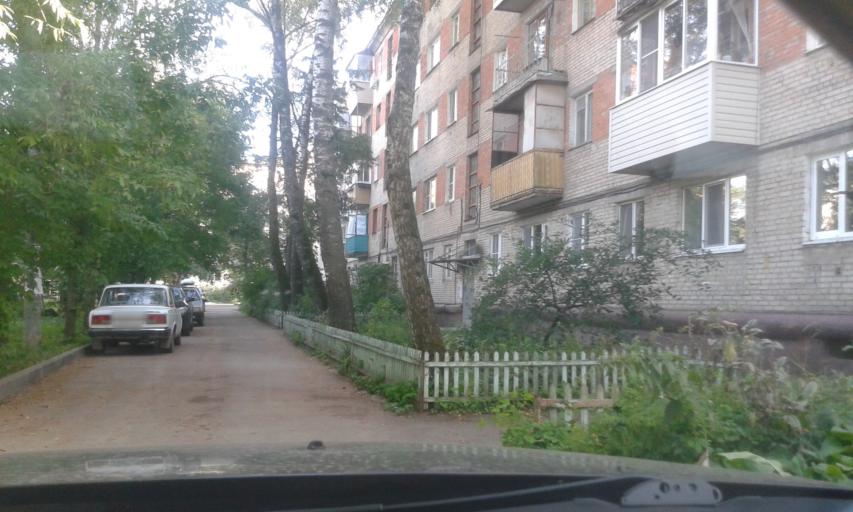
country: RU
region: Tula
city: Tula
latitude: 54.1872
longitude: 37.5954
